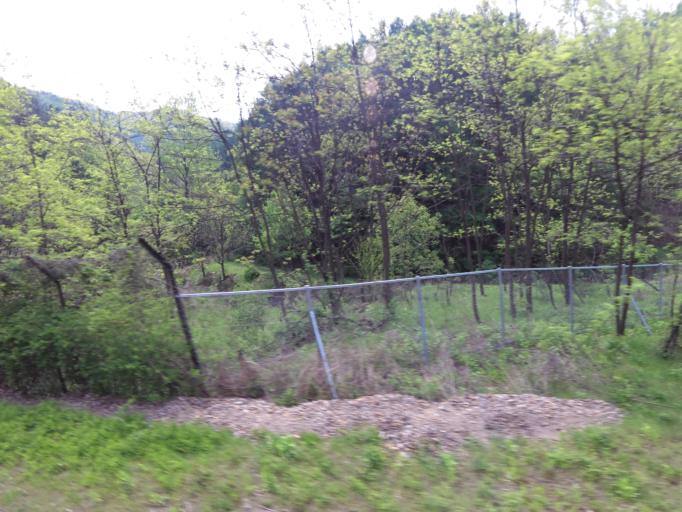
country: KR
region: Daejeon
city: Daejeon
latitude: 36.3389
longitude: 127.4967
